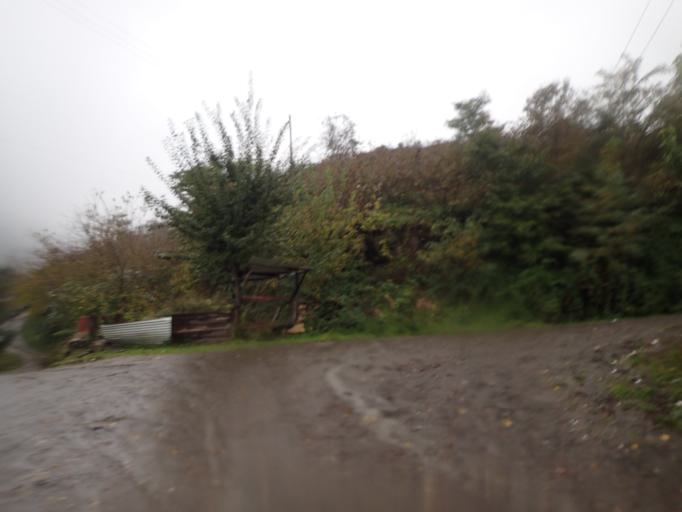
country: TR
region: Ordu
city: Persembe
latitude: 41.0300
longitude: 37.7235
